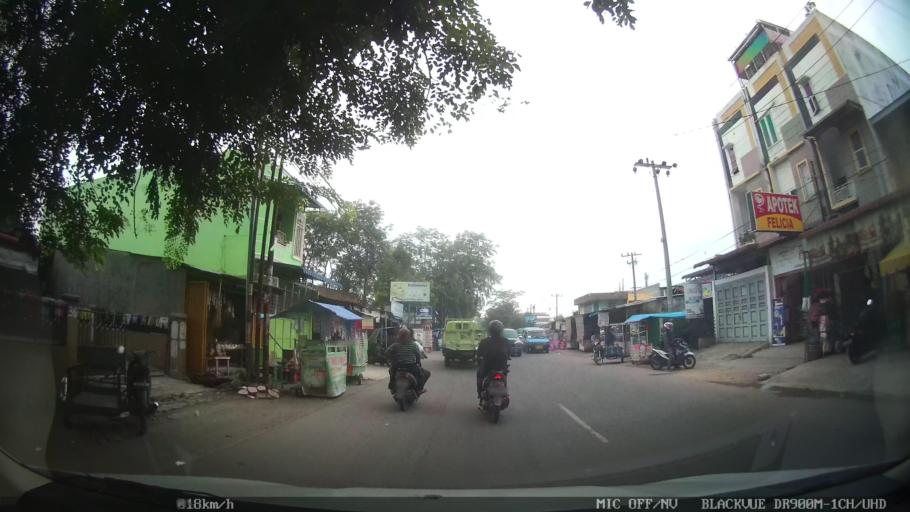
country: ID
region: North Sumatra
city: Medan
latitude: 3.5585
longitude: 98.7030
